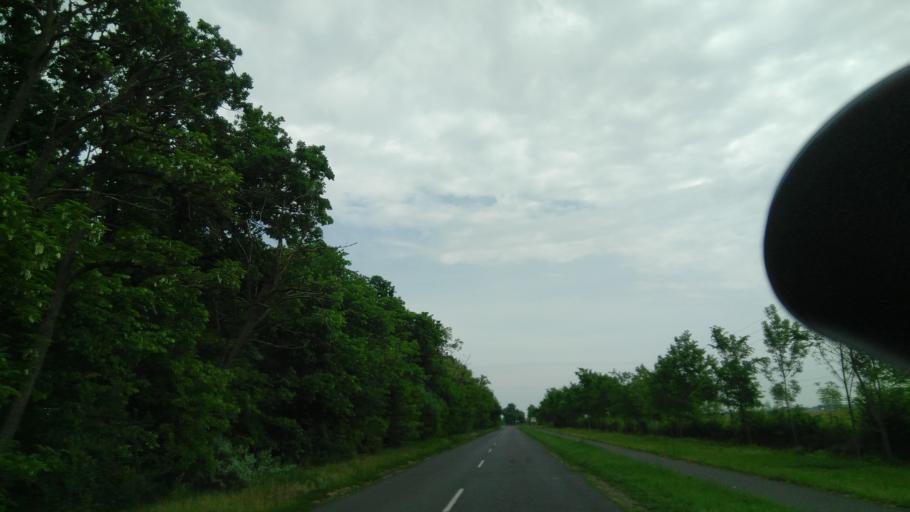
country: HU
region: Bekes
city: Szeghalom
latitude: 47.0496
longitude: 21.1912
